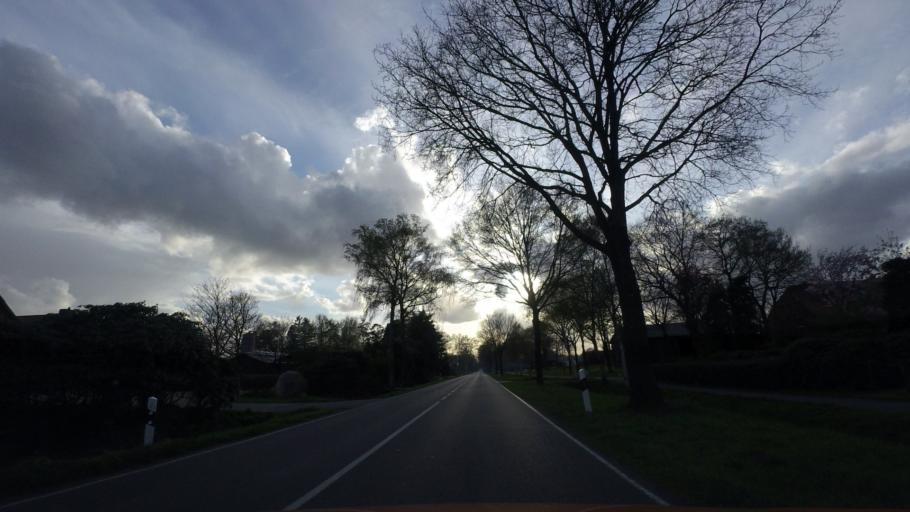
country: DE
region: Lower Saxony
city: Edewecht
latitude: 53.1233
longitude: 8.0600
